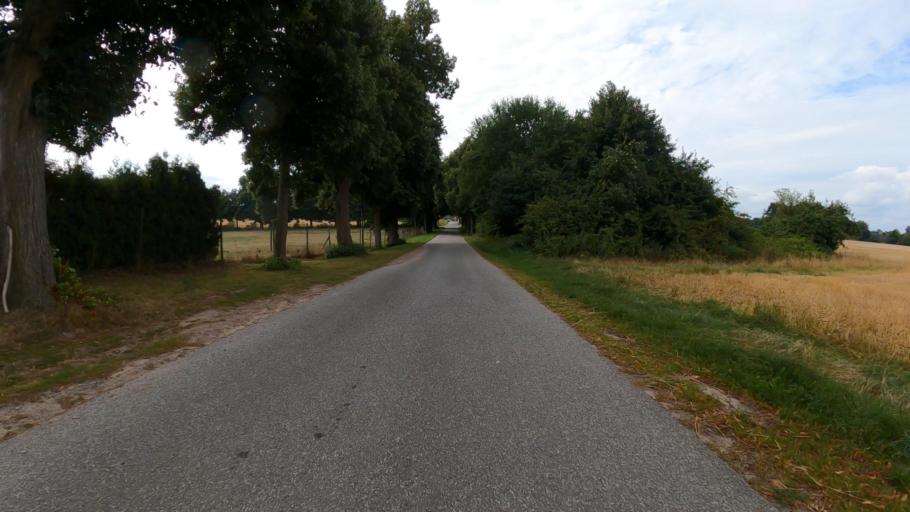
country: DE
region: Lower Saxony
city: Neu Wulmstorf
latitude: 53.4286
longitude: 9.8018
